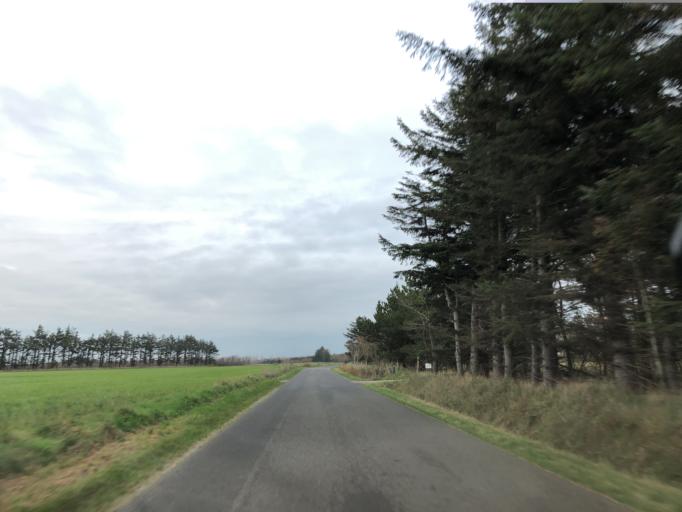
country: DK
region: Central Jutland
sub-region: Holstebro Kommune
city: Ulfborg
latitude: 56.2707
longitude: 8.2563
